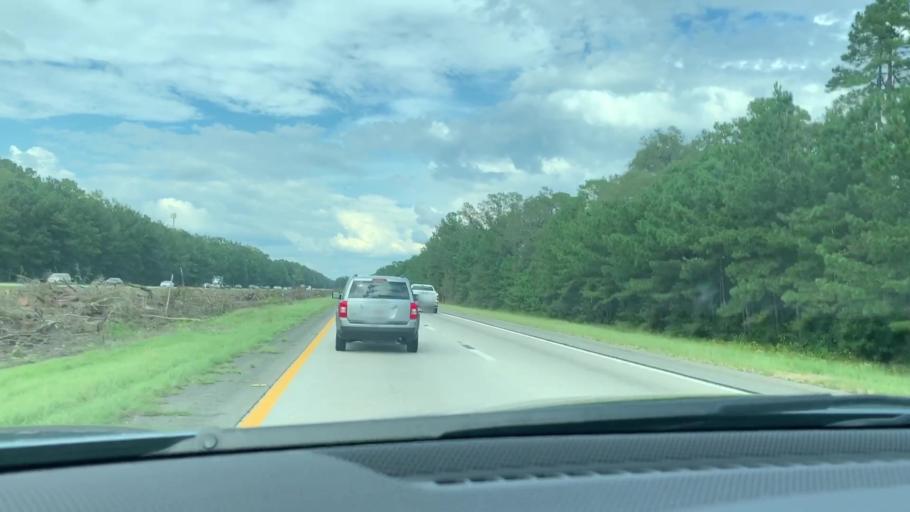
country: US
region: South Carolina
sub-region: Jasper County
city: Hardeeville
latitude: 32.3812
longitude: -81.0282
